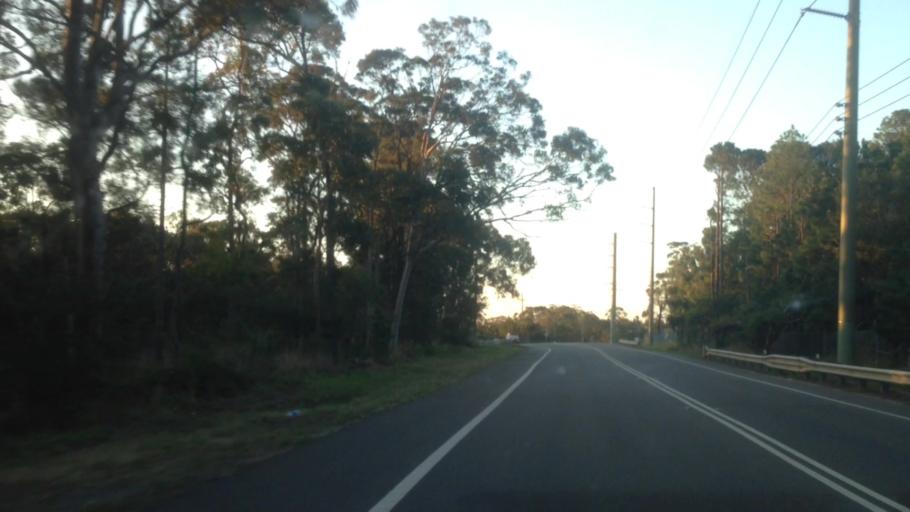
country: AU
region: New South Wales
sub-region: Wyong Shire
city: Kingfisher Shores
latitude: -33.1749
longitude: 151.5396
